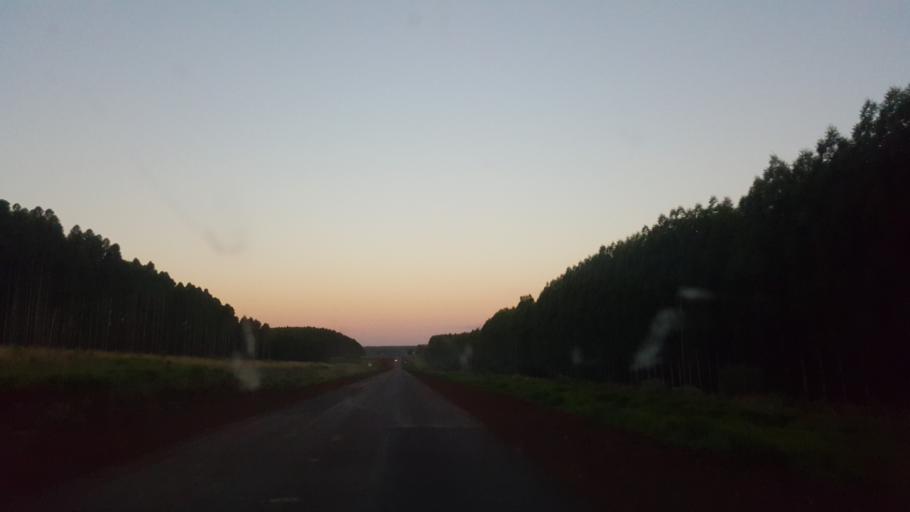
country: AR
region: Corrientes
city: Garruchos
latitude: -28.2467
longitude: -55.8406
